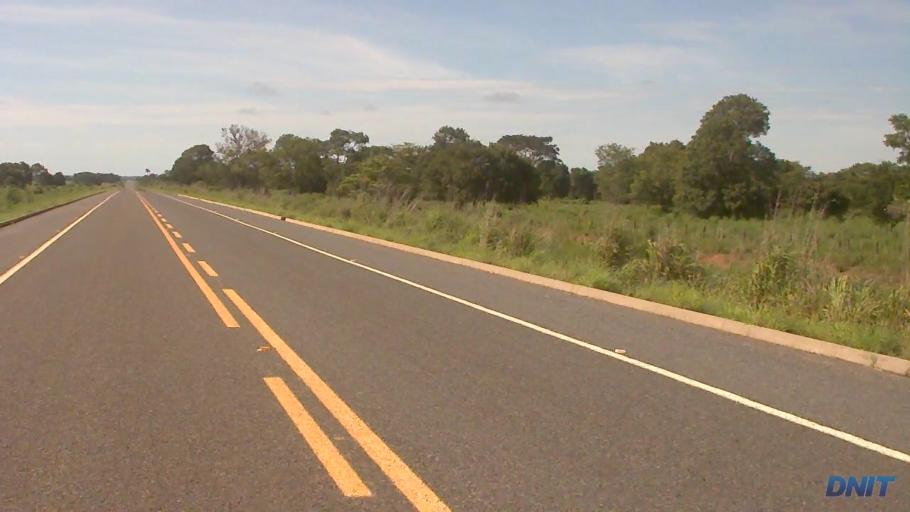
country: BR
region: Goias
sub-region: Sao Miguel Do Araguaia
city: Sao Miguel do Araguaia
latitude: -13.4362
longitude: -50.1248
